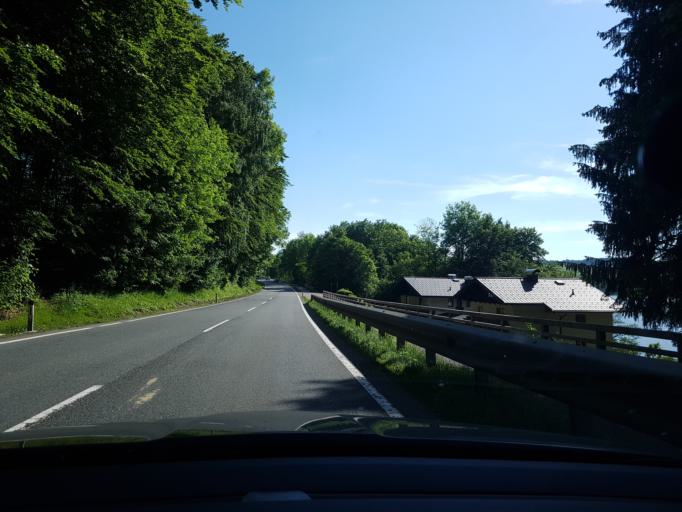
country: AT
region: Salzburg
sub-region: Politischer Bezirk Salzburg-Umgebung
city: Mattsee
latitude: 47.9594
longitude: 13.0938
